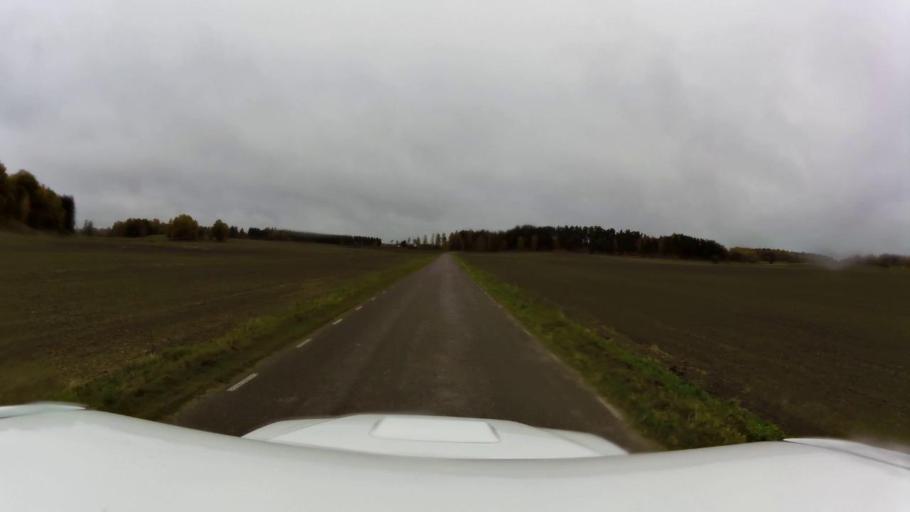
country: SE
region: OEstergoetland
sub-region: Norrkopings Kommun
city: Kimstad
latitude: 58.3940
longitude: 15.9497
